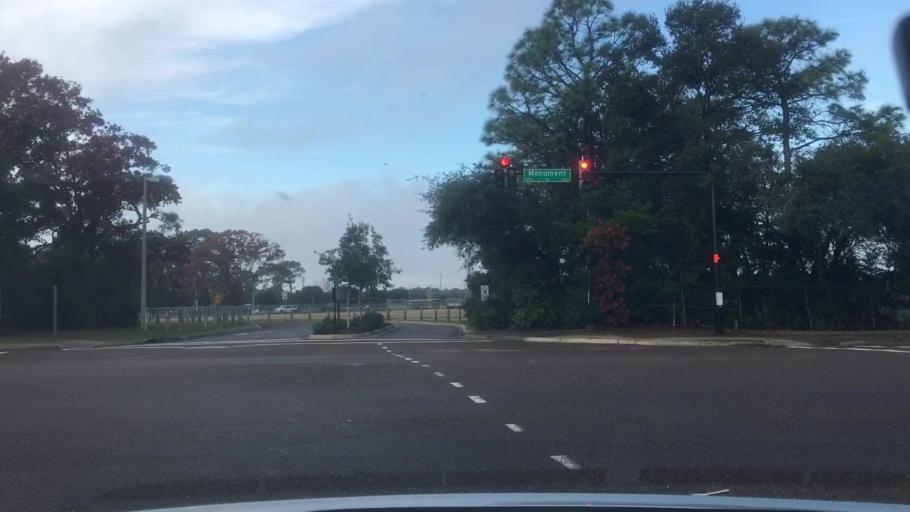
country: US
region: Florida
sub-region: Duval County
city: Atlantic Beach
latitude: 30.3635
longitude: -81.5027
